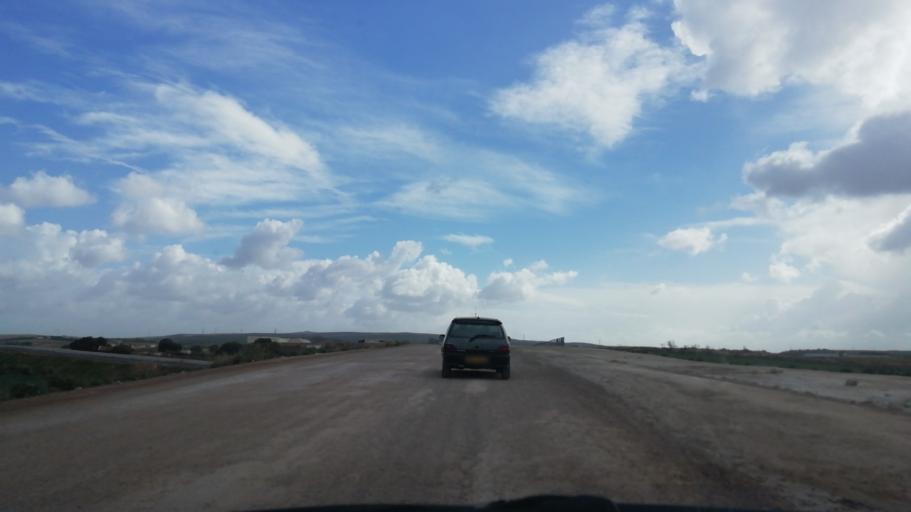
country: DZ
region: Oran
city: Sidi ech Chahmi
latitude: 35.6356
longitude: -0.5394
